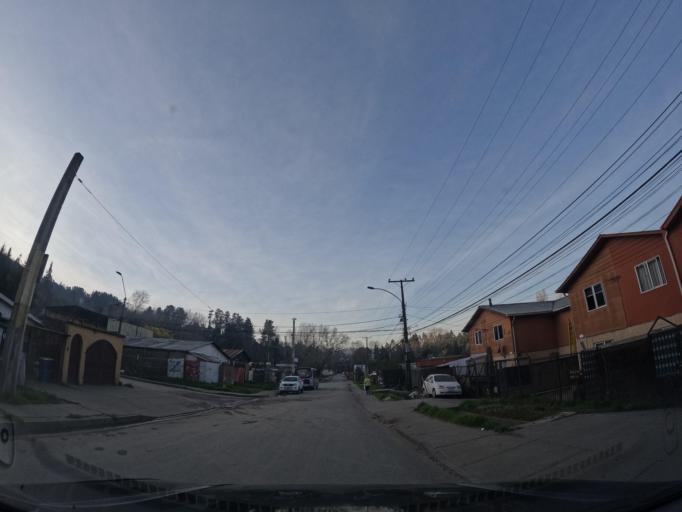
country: CL
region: Biobio
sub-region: Provincia de Concepcion
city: Concepcion
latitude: -36.8439
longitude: -73.0096
